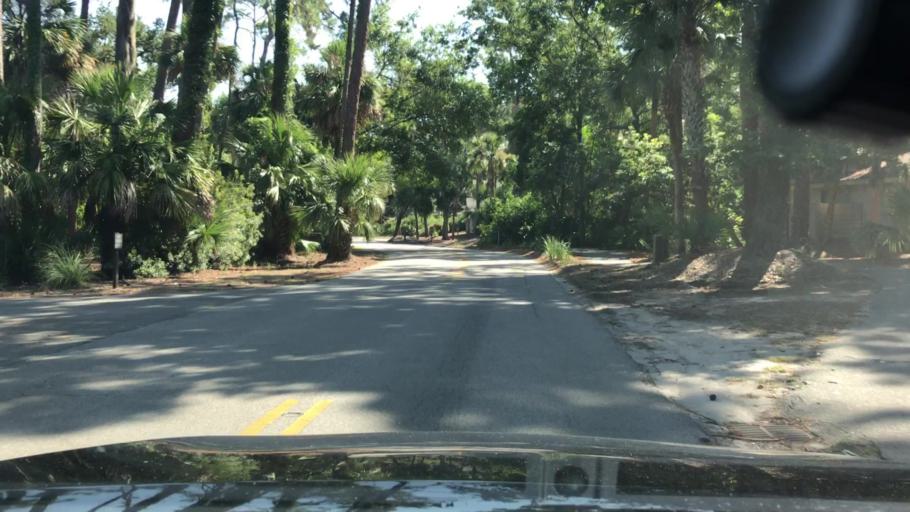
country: US
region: South Carolina
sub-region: Beaufort County
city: Hilton Head Island
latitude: 32.1287
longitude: -80.7832
